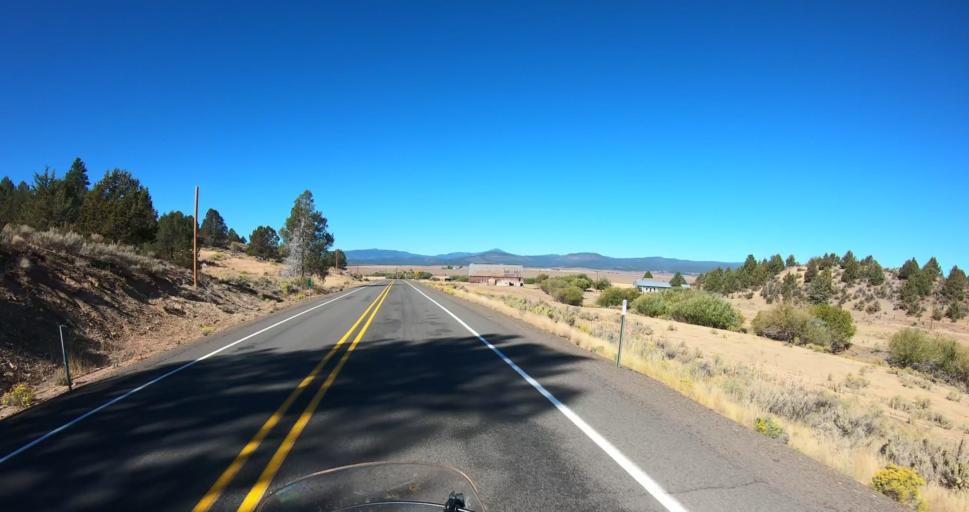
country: US
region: Oregon
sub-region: Lake County
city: Lakeview
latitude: 42.2621
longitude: -120.3430
